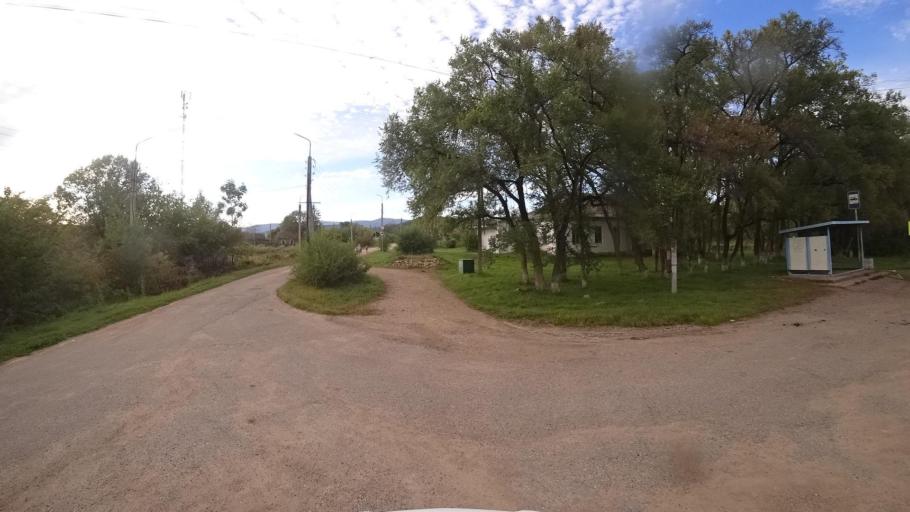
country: RU
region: Primorskiy
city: Dostoyevka
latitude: 44.3459
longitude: 133.4135
